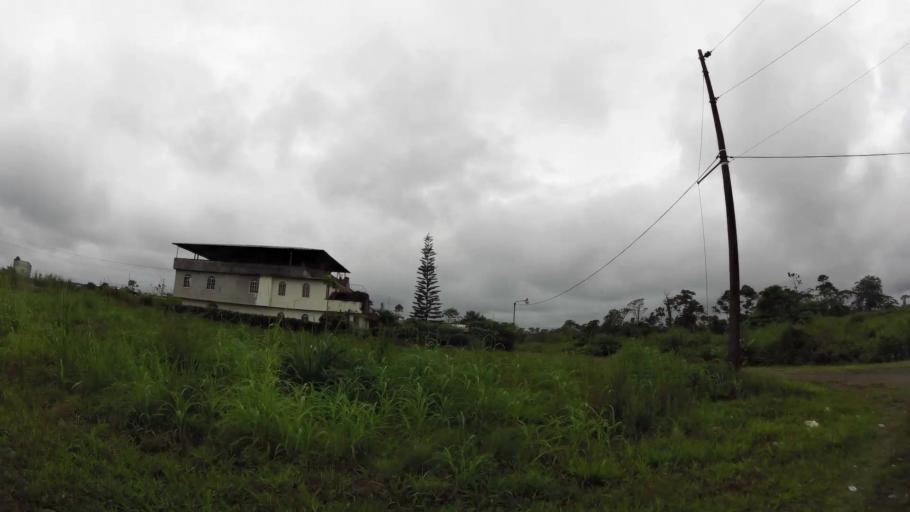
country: EC
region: Santo Domingo de los Tsachilas
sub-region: Canton Santo Domingo de los Colorados
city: Santo Domingo de los Colorados
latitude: -0.2515
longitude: -79.1430
